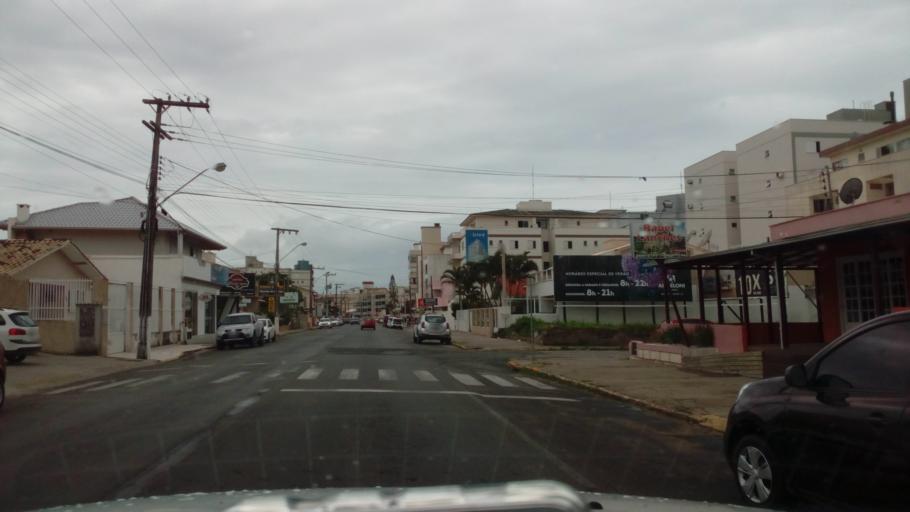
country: BR
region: Santa Catarina
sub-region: Laguna
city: Laguna
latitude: -28.4874
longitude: -48.7701
